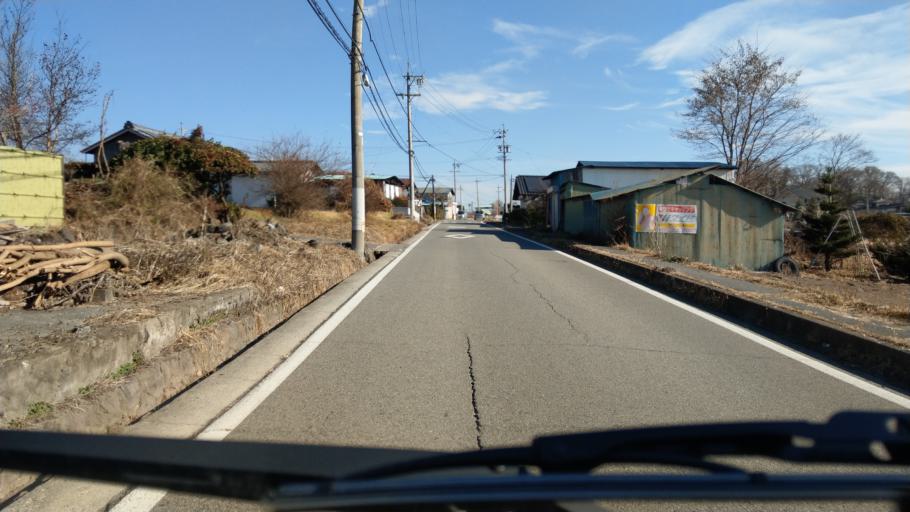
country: JP
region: Nagano
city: Komoro
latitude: 36.3060
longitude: 138.4552
